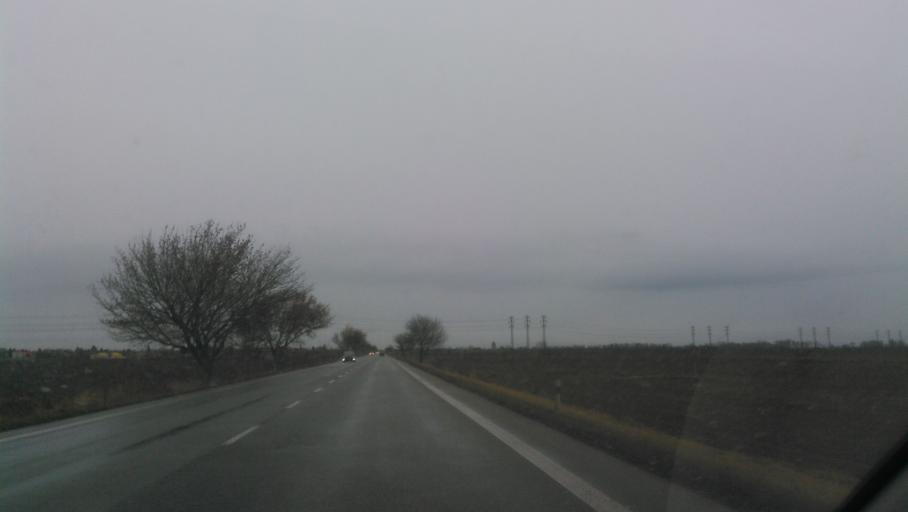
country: SK
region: Nitriansky
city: Sellye
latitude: 48.1762
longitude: 17.8225
